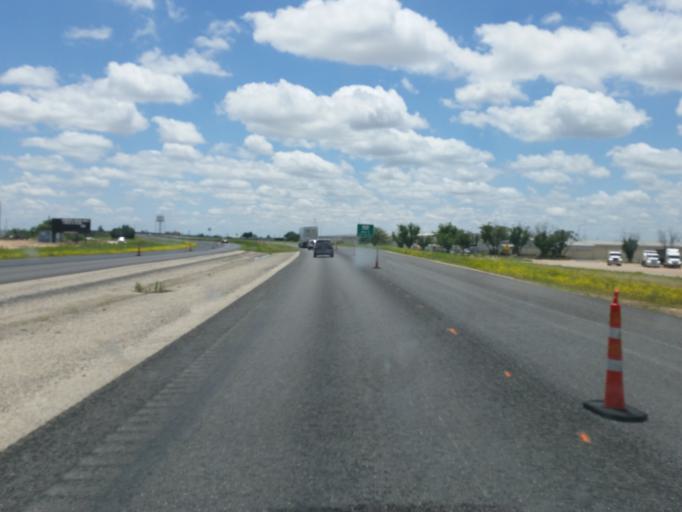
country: US
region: Texas
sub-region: Scurry County
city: Snyder
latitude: 32.7438
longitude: -100.9228
